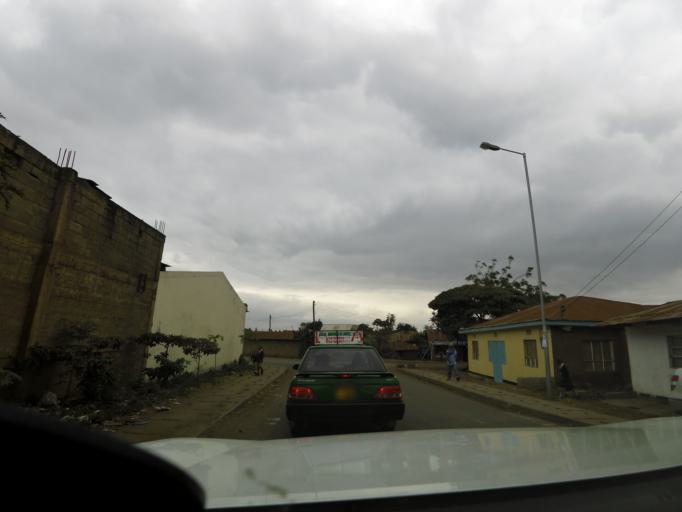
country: TZ
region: Arusha
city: Arusha
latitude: -3.3683
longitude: 36.6605
